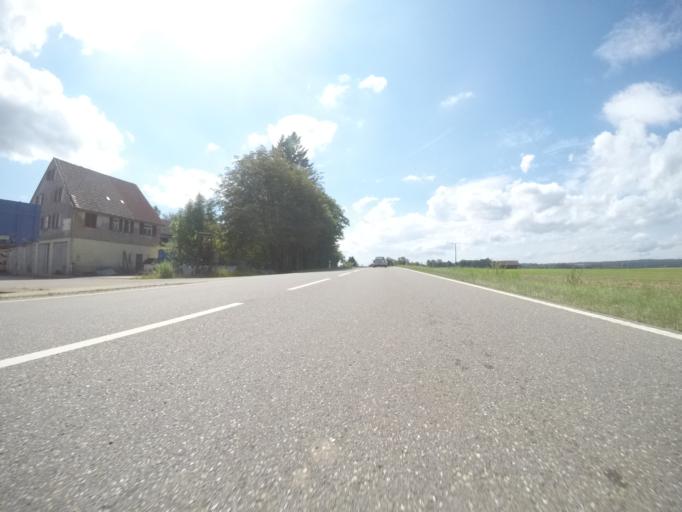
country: DE
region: Baden-Wuerttemberg
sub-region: Karlsruhe Region
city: Pfalzgrafenweiler
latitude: 48.5319
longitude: 8.5600
